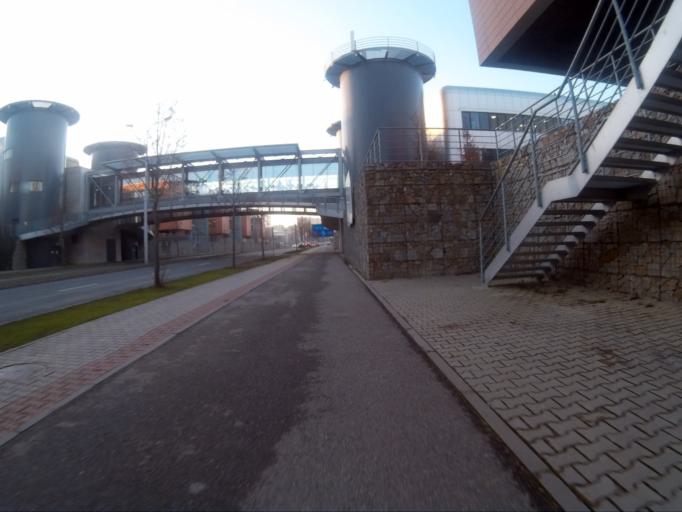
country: CZ
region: South Moravian
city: Ostopovice
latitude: 49.1779
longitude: 16.5715
